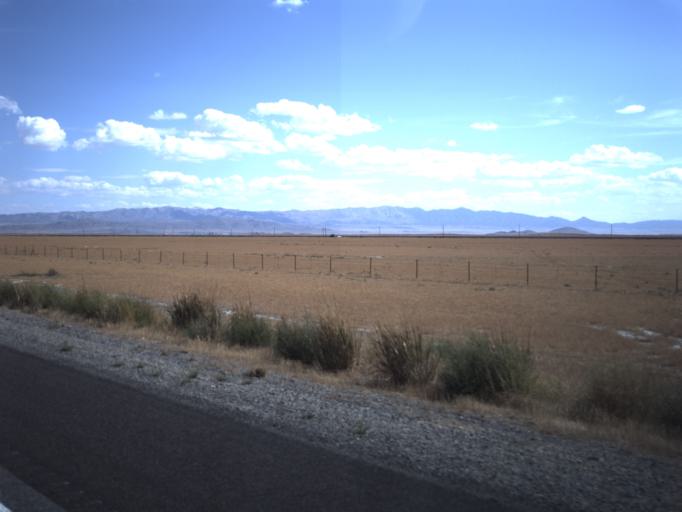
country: US
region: Utah
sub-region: Tooele County
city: Grantsville
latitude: 40.7263
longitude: -113.2439
